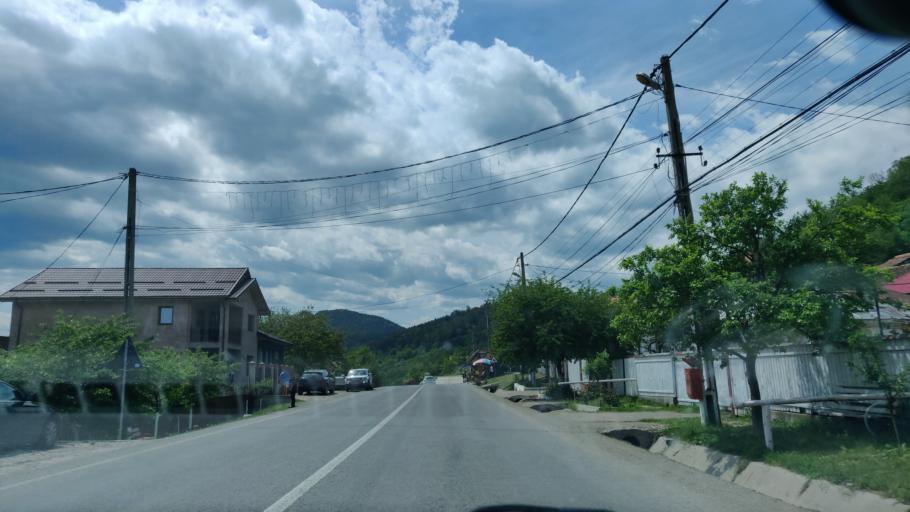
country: RO
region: Vrancea
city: Matacina
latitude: 45.8892
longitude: 26.8201
